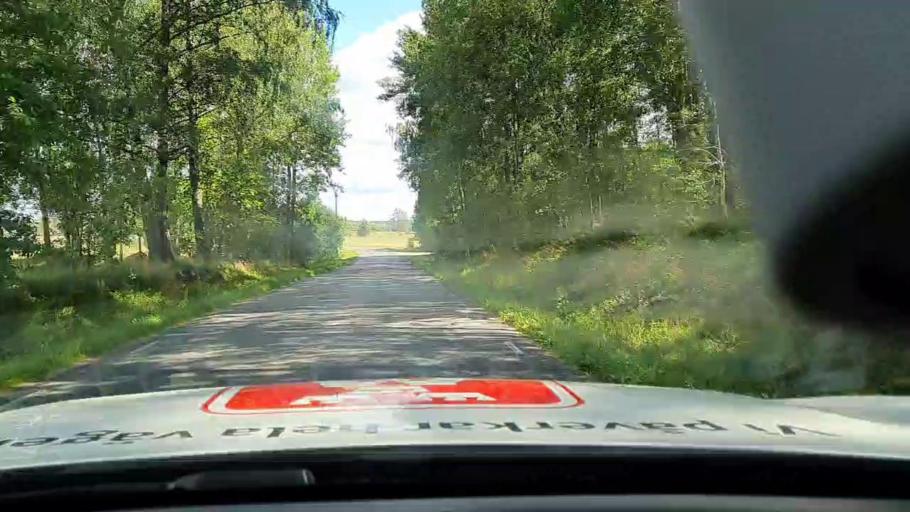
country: SE
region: Vaestra Goetaland
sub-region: Toreboda Kommun
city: Toereboda
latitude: 58.5709
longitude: 14.0670
